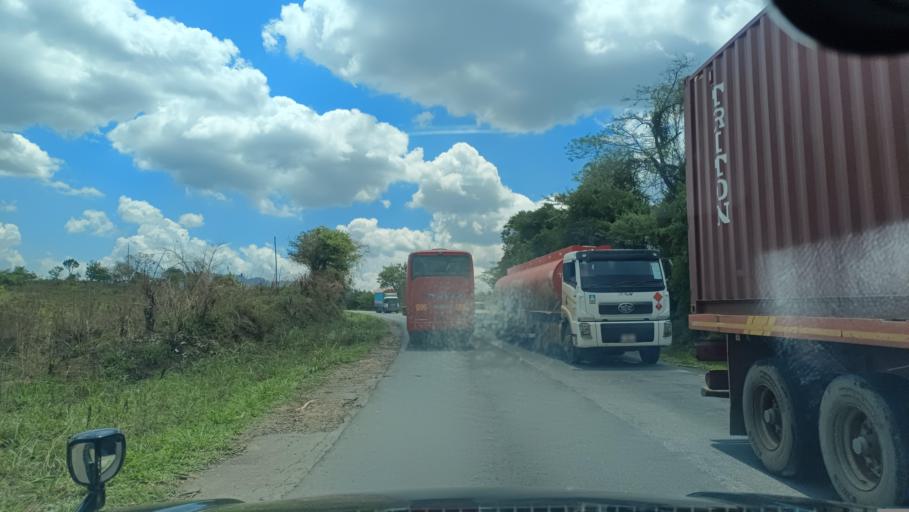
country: TZ
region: Morogoro
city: Mikumi
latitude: -7.4558
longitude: 36.9206
